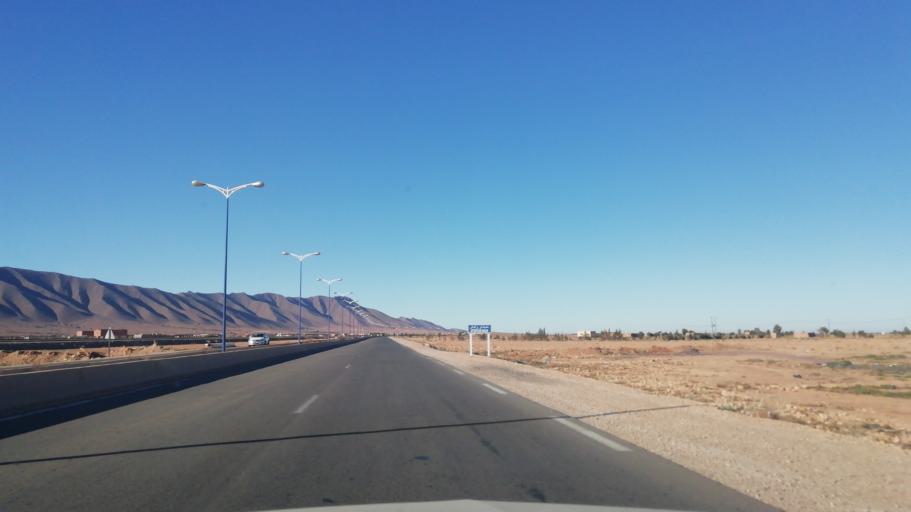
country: DZ
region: Wilaya de Naama
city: Naama
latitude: 33.5632
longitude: -0.2383
